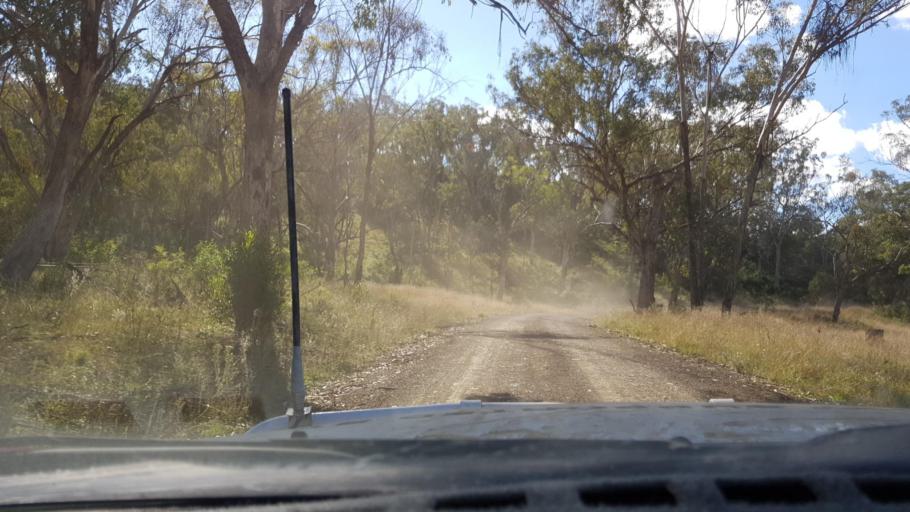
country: AU
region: New South Wales
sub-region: Tamworth Municipality
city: Manilla
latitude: -30.4791
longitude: 150.7709
